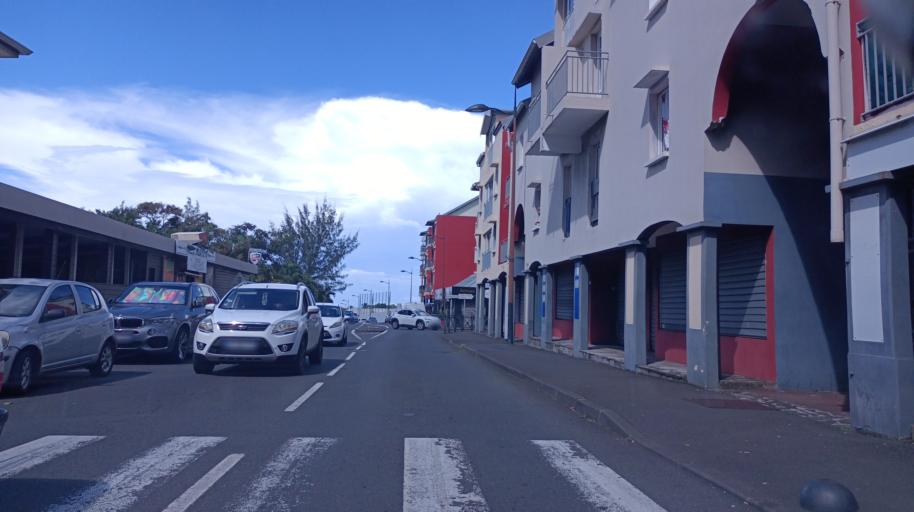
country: RE
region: Reunion
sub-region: Reunion
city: Saint-Joseph
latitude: -21.3769
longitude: 55.6152
